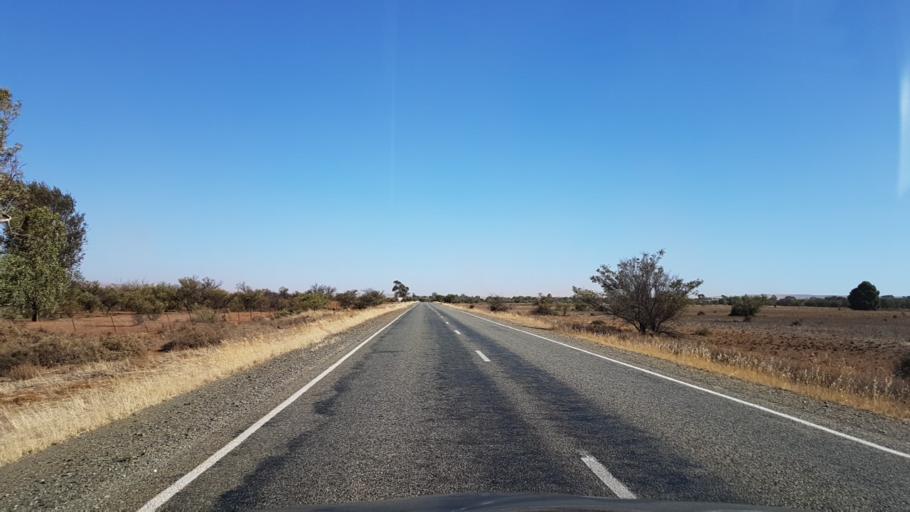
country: AU
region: South Australia
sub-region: Peterborough
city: Peterborough
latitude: -33.1416
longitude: 138.9304
